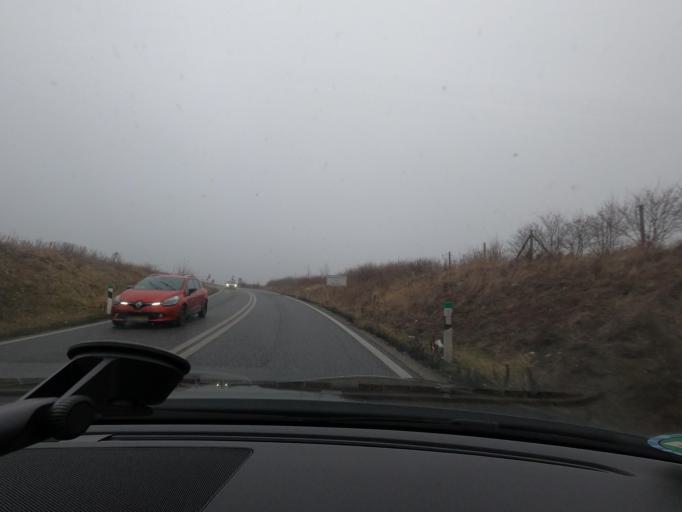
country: DE
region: North Rhine-Westphalia
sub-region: Regierungsbezirk Koln
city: Merzenich
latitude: 50.8486
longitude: 6.5170
